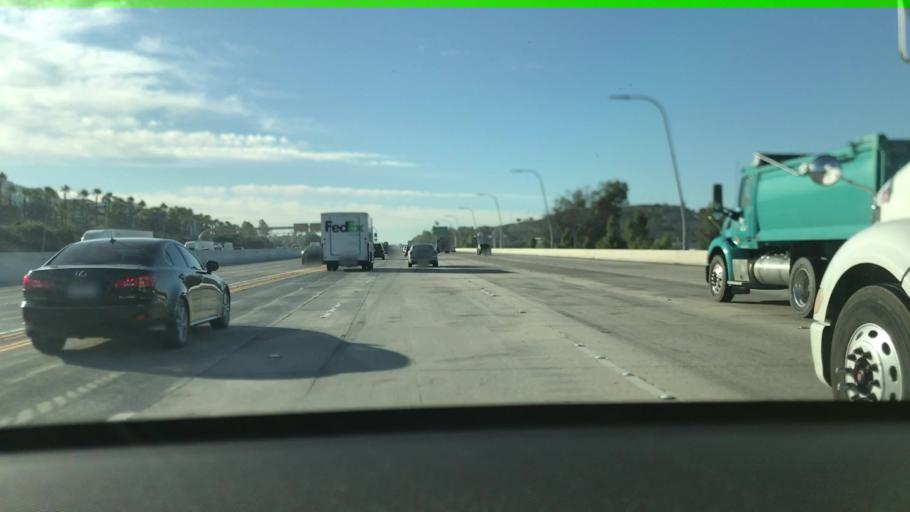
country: US
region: California
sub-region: San Diego County
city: Escondido
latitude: 33.1144
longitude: -117.0986
